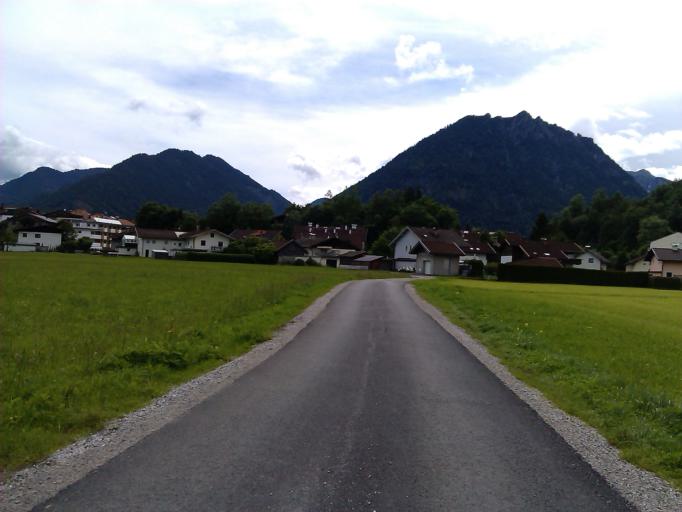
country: AT
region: Tyrol
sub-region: Politischer Bezirk Reutte
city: Lechaschau
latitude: 47.4914
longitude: 10.7123
